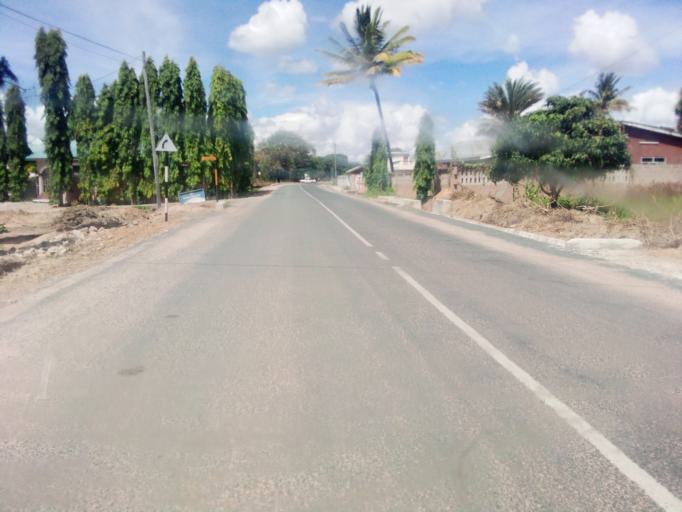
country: TZ
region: Dodoma
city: Kisasa
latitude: -6.1648
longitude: 35.7700
